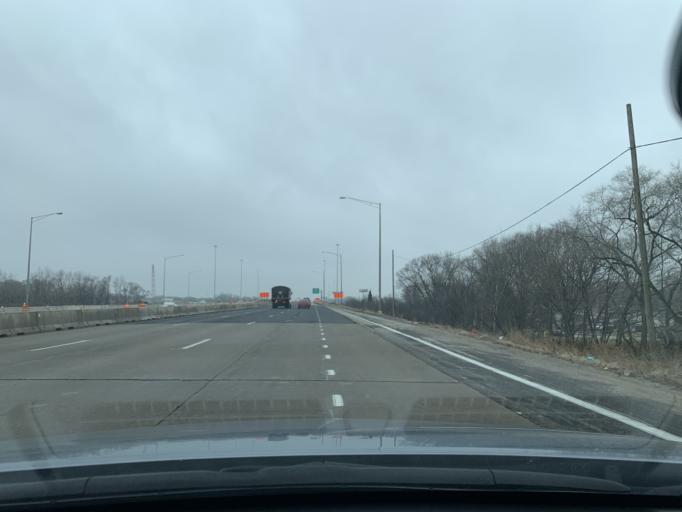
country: US
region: Illinois
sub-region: Cook County
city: Posen
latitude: 41.6217
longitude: -87.6833
